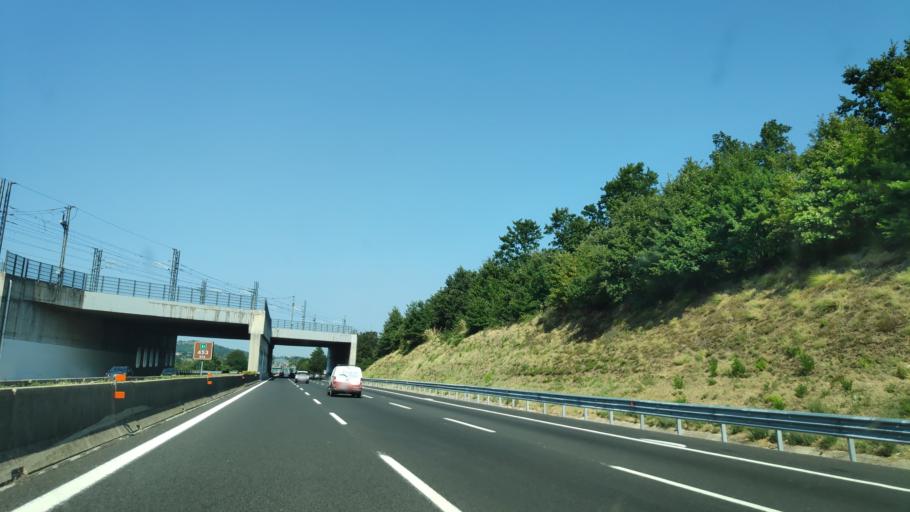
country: IT
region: Campania
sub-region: Provincia di Caserta
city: Bivio Mortola
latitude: 41.4230
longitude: 13.9231
